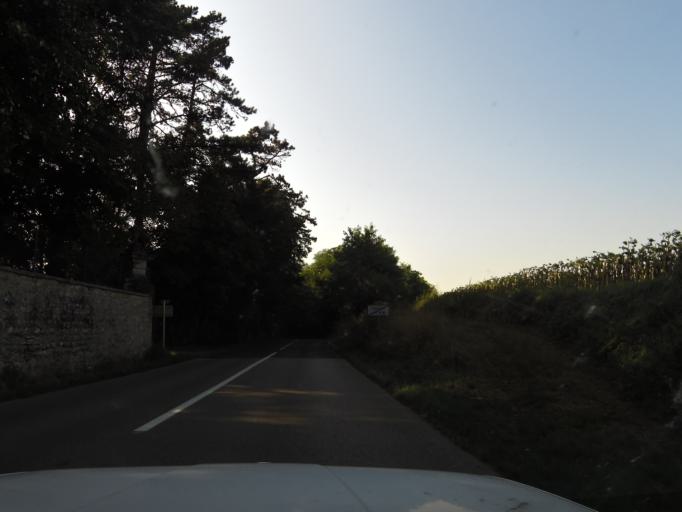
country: FR
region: Rhone-Alpes
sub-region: Departement de l'Ain
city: Chazey-sur-Ain
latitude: 45.8968
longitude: 5.2530
